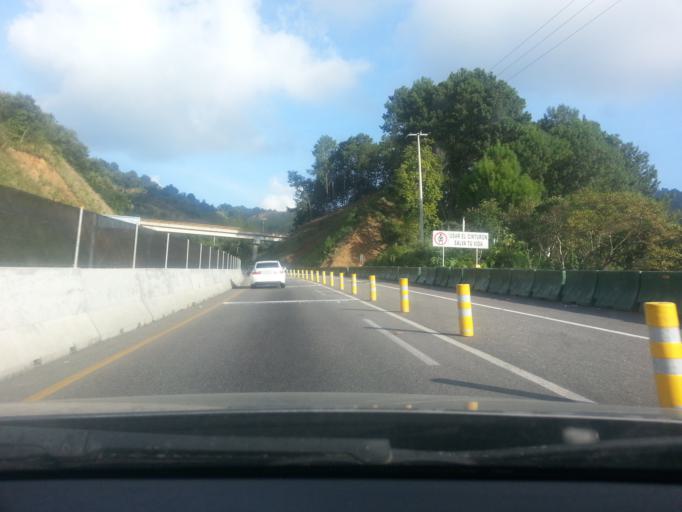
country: MX
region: Puebla
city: Necaxa
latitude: 20.2371
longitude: -98.0324
